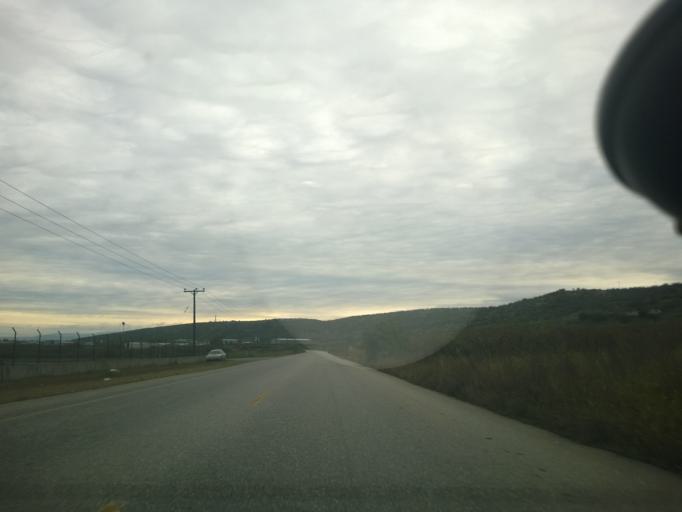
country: GR
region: Central Macedonia
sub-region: Nomos Pellis
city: Profitis Ilias
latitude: 40.8121
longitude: 22.1460
